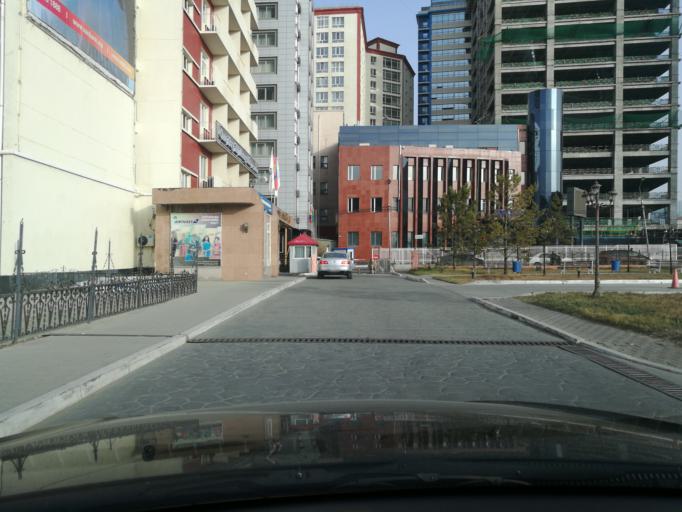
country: MN
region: Ulaanbaatar
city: Ulaanbaatar
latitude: 47.9125
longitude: 106.9144
